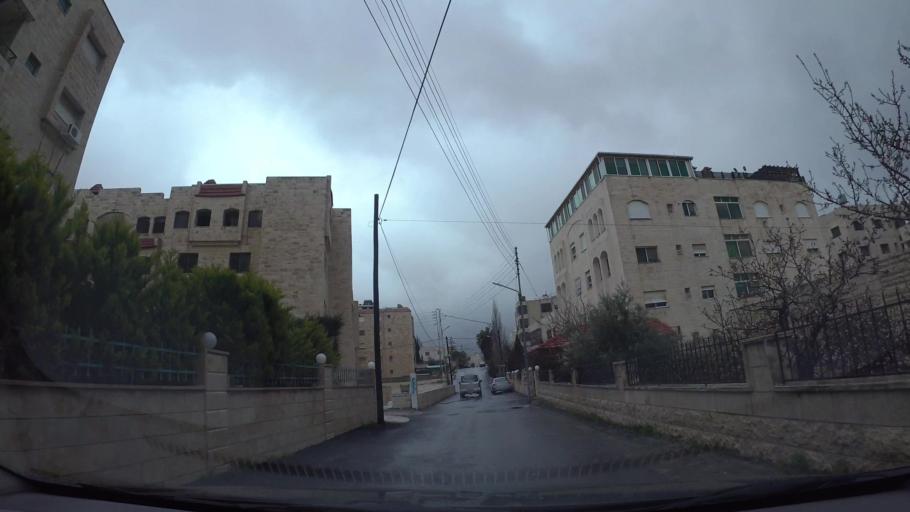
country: JO
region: Amman
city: Al Jubayhah
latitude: 32.0293
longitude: 35.8733
